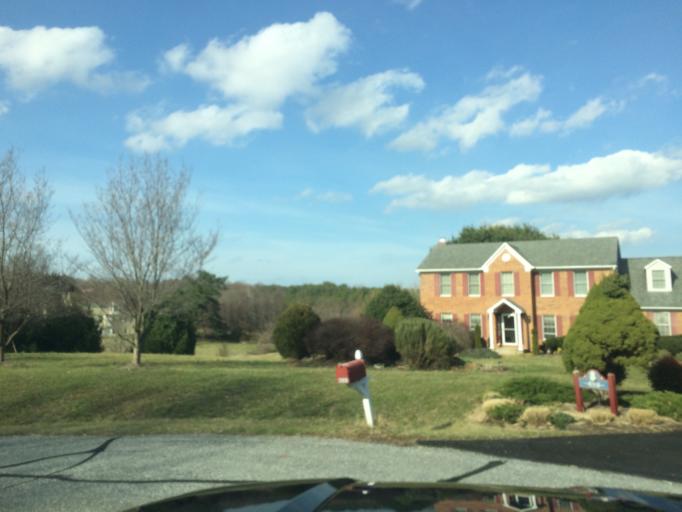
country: US
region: Maryland
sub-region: Howard County
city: Highland
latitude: 39.2404
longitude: -76.9788
